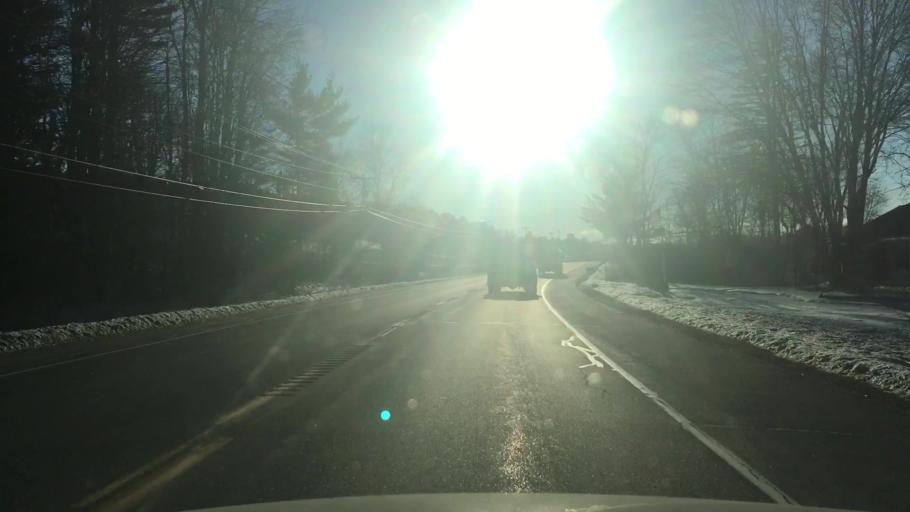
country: US
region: Maine
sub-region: Somerset County
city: Norridgewock
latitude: 44.7346
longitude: -69.7613
